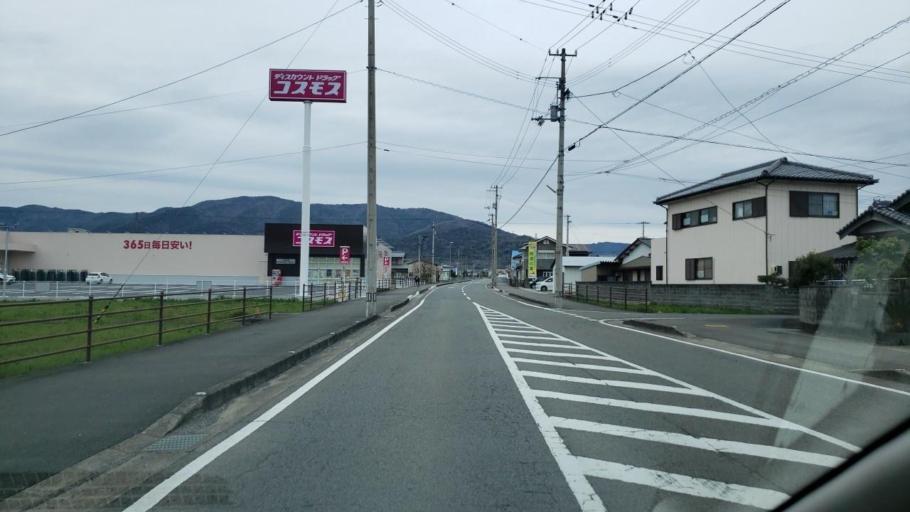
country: JP
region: Tokushima
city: Kamojimacho-jogejima
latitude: 34.1015
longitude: 134.3413
